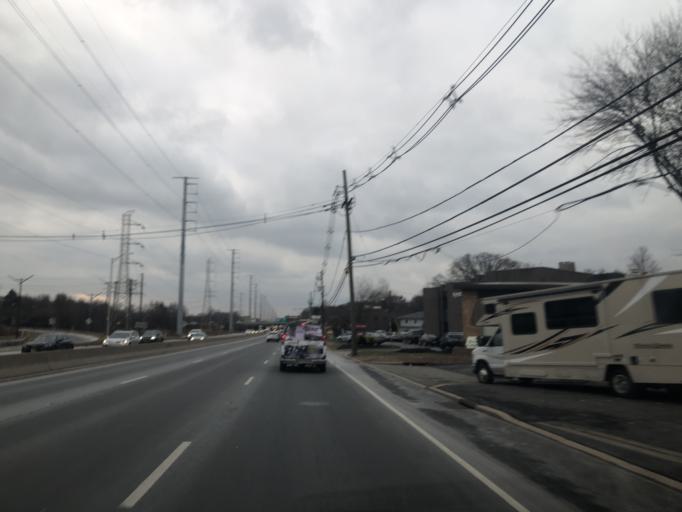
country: US
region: New Jersey
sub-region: Middlesex County
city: Metuchen
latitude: 40.5319
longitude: -74.3498
